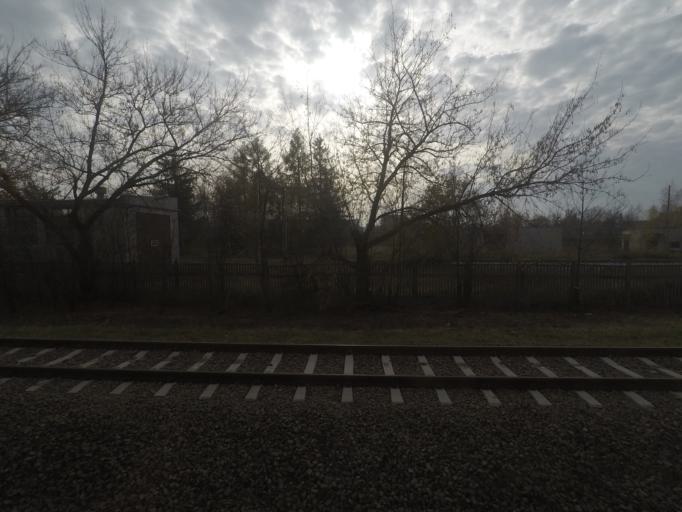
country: PL
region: Subcarpathian Voivodeship
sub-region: Powiat ropczycko-sedziszowski
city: Ostrow
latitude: 50.0793
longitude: 21.5892
